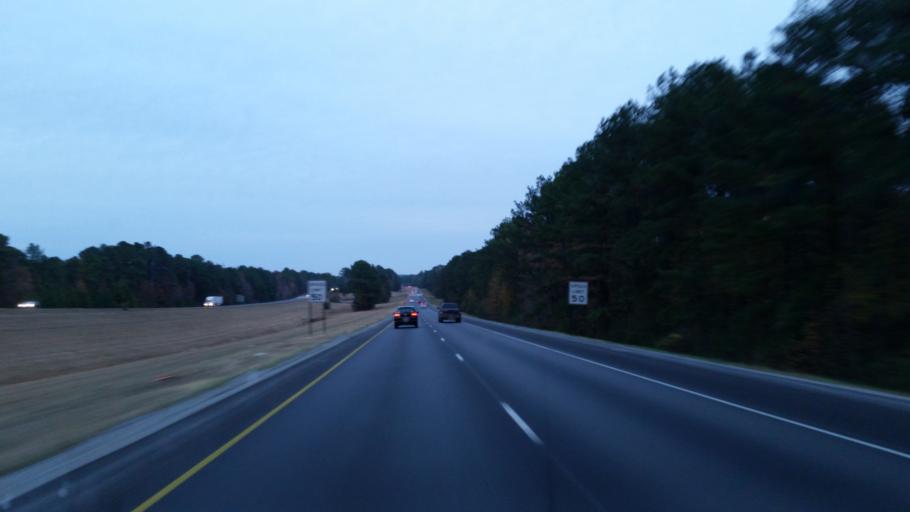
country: US
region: Alabama
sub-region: Hale County
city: Moundville
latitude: 32.9941
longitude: -87.7774
